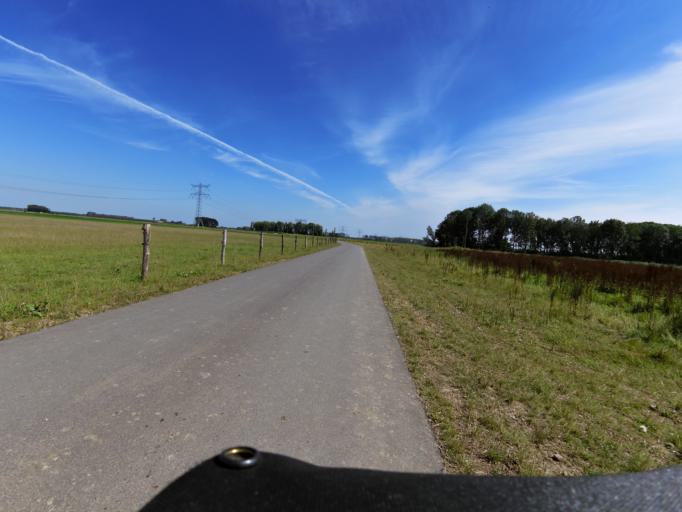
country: NL
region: South Holland
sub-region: Gemeente Hardinxveld-Giessendam
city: Neder-Hardinxveld
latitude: 51.7789
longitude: 4.8204
